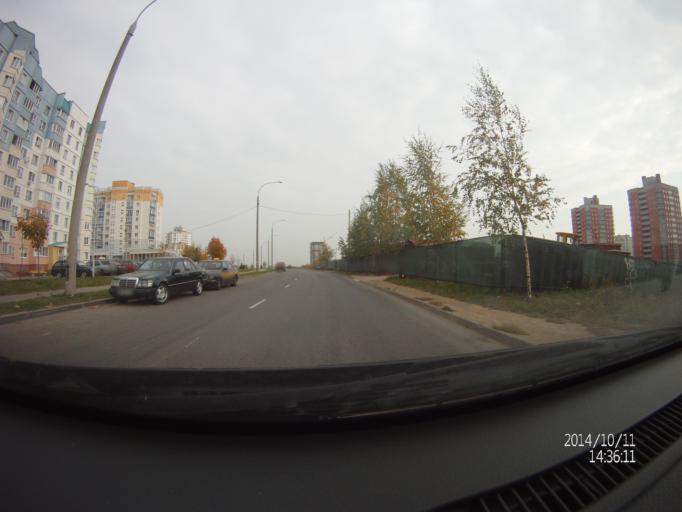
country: BY
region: Minsk
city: Novoye Medvezhino
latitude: 53.8774
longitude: 27.4514
